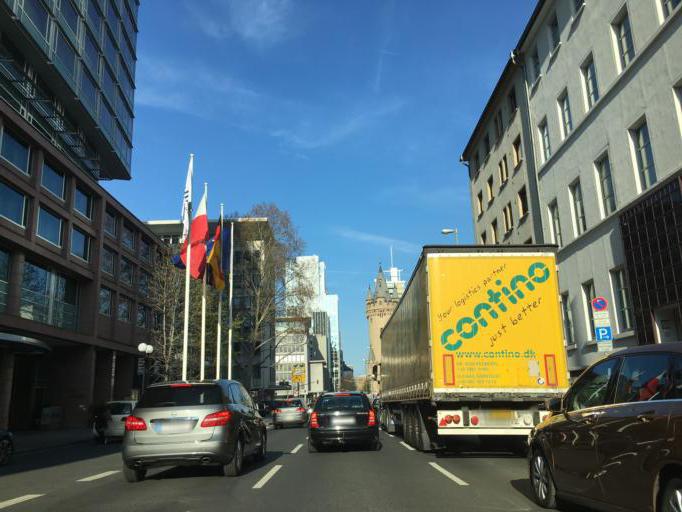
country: DE
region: Hesse
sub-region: Regierungsbezirk Darmstadt
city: Frankfurt am Main
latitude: 50.1165
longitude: 8.6770
